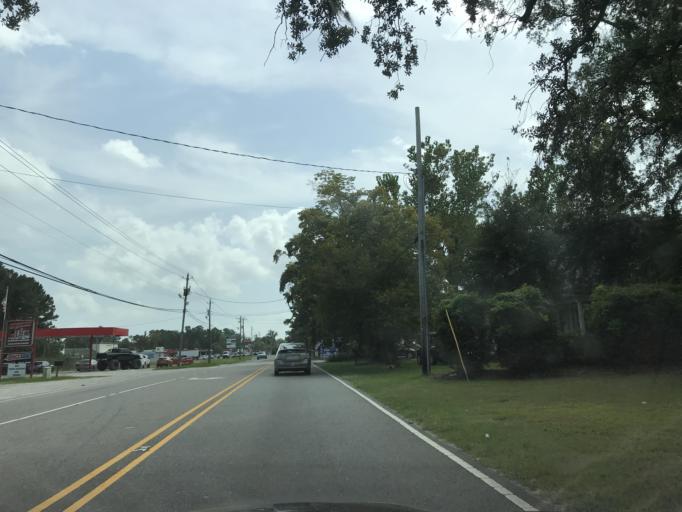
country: US
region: North Carolina
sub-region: New Hanover County
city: Wrightsboro
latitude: 34.2766
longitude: -77.9251
